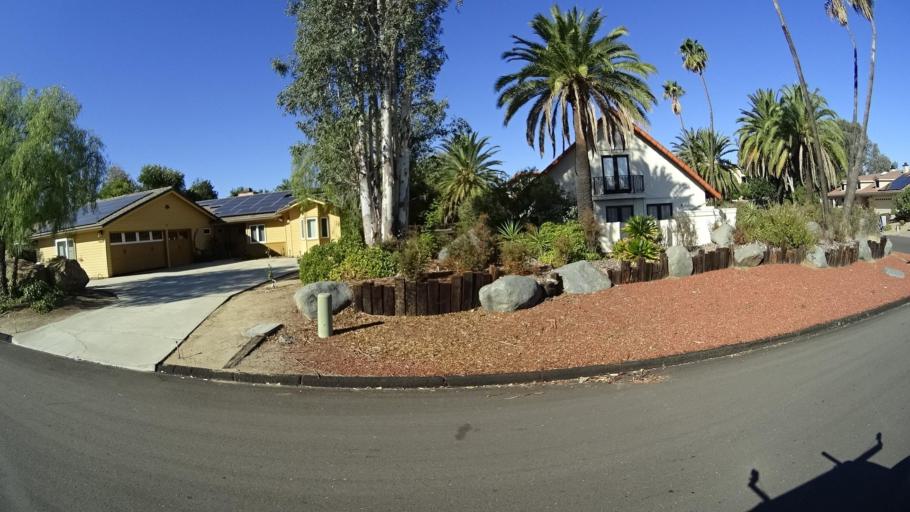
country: US
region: California
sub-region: San Diego County
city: San Diego Country Estates
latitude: 32.9976
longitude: -116.8181
